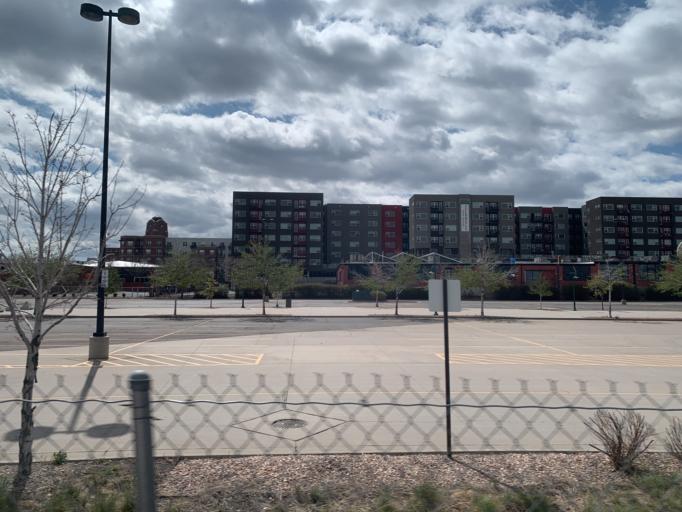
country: US
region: Colorado
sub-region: Denver County
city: Denver
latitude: 39.7600
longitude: -104.9903
